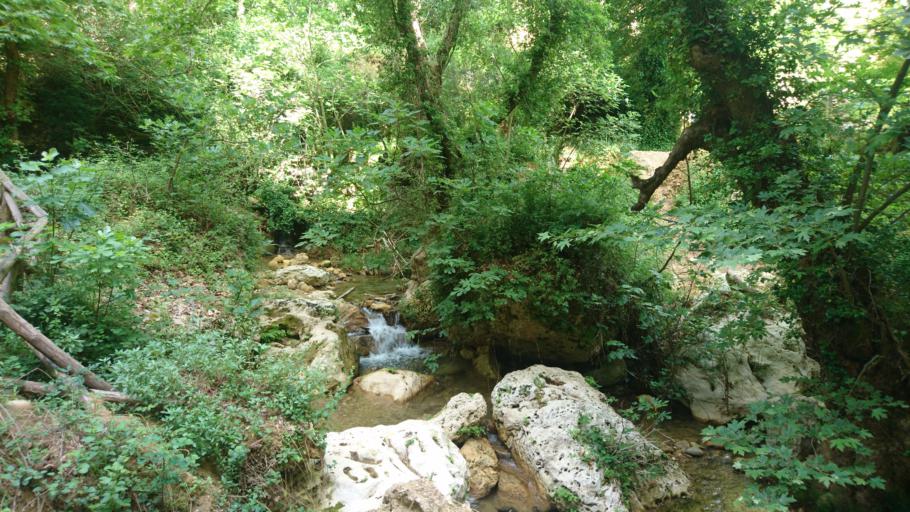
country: GR
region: Crete
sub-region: Nomos Rethymnis
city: Rethymno
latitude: 35.3483
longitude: 24.5093
